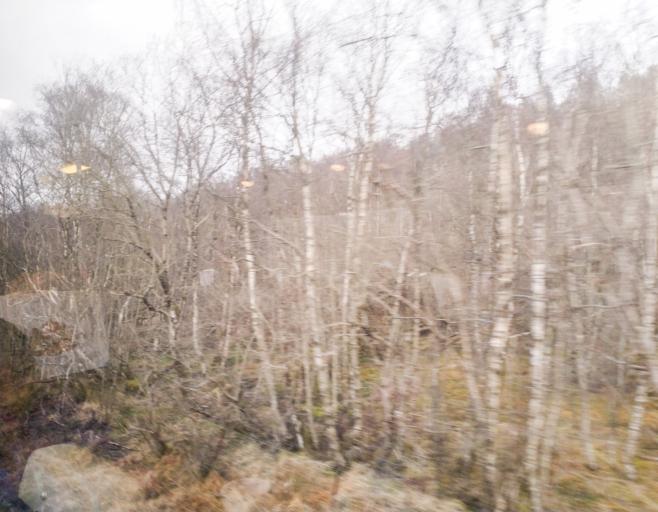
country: GB
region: Scotland
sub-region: Highland
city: Spean Bridge
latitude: 56.8859
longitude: -4.8189
